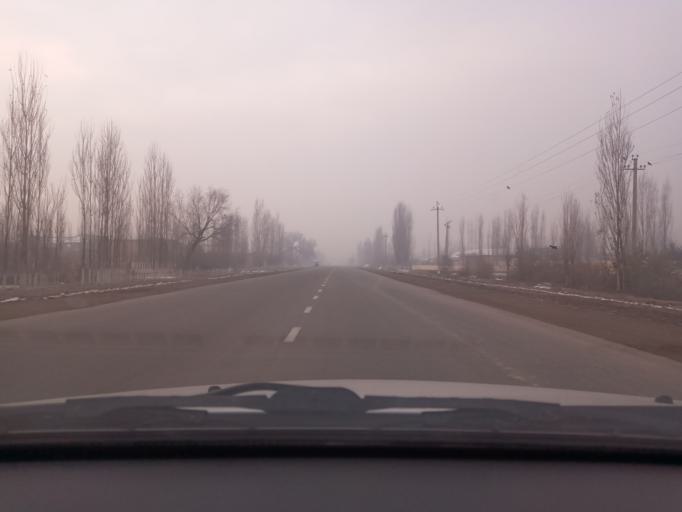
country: UZ
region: Namangan
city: Pop
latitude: 40.8905
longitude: 71.1471
